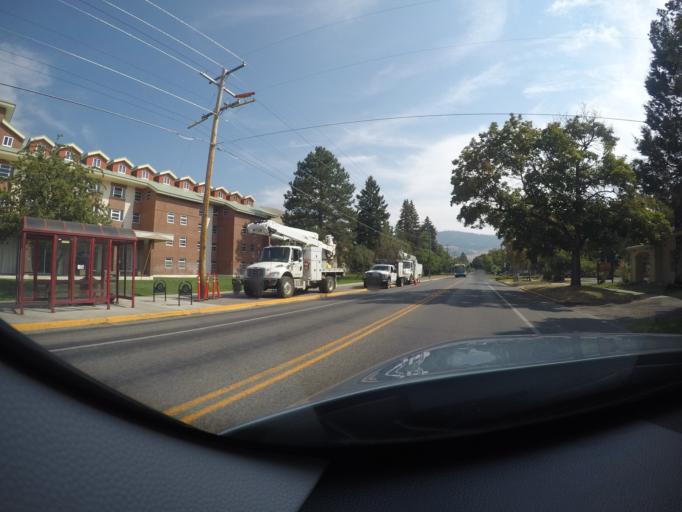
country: US
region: Montana
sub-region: Missoula County
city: Missoula
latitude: 46.8587
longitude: -113.9893
